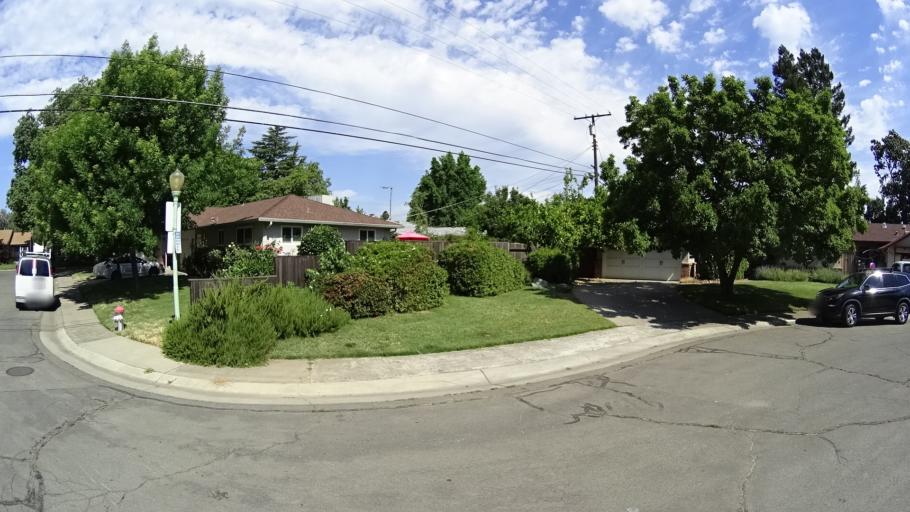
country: US
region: California
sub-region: Sacramento County
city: Sacramento
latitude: 38.5794
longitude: -121.4350
